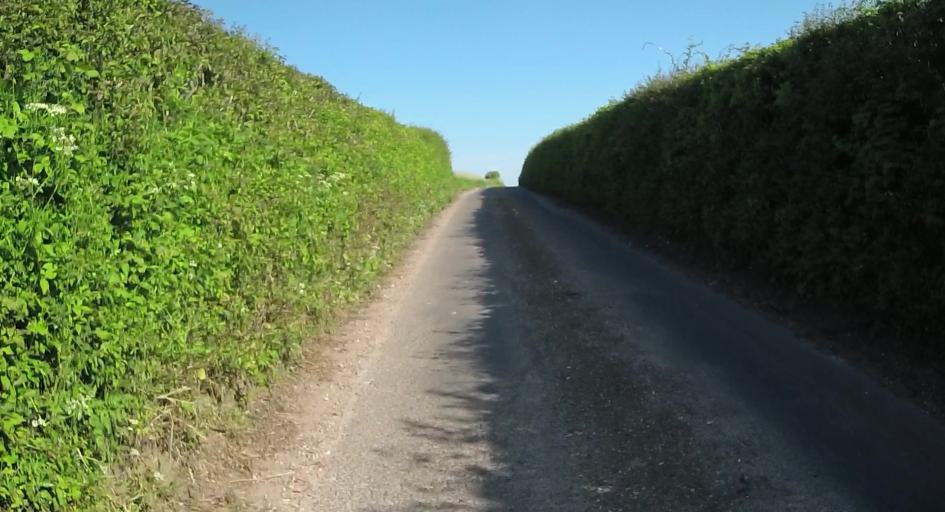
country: GB
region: England
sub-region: Hampshire
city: Overton
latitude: 51.1749
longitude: -1.1999
